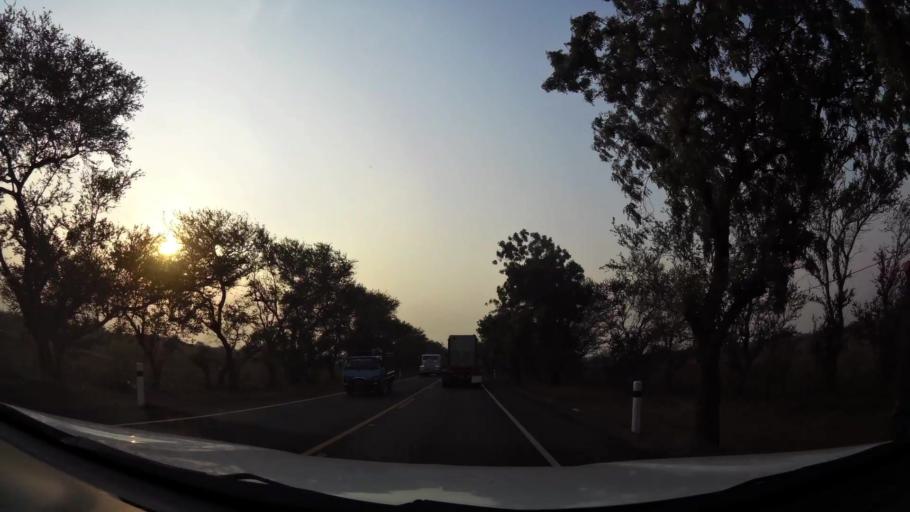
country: NI
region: Leon
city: Nagarote
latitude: 12.2805
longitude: -86.5795
